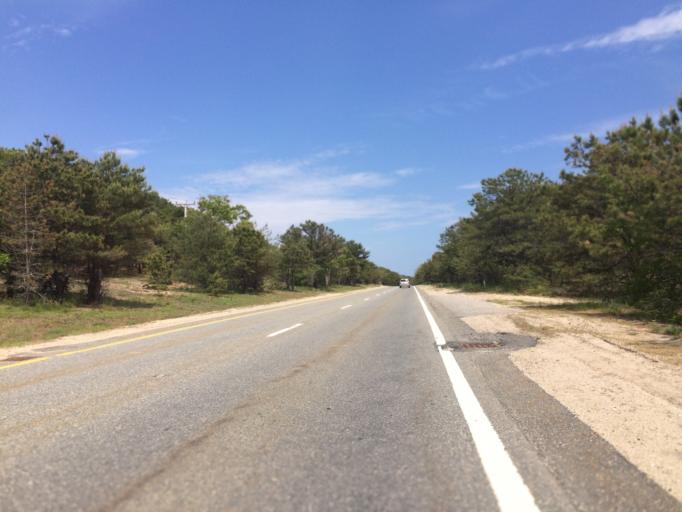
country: US
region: Massachusetts
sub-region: Barnstable County
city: Provincetown
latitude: 42.0632
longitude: -70.1776
